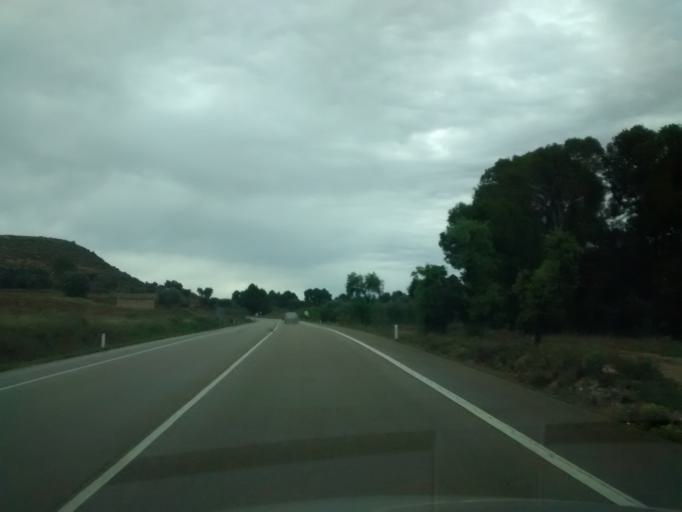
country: ES
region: Aragon
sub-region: Provincia de Zaragoza
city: Caspe
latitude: 41.2131
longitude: 0.0077
